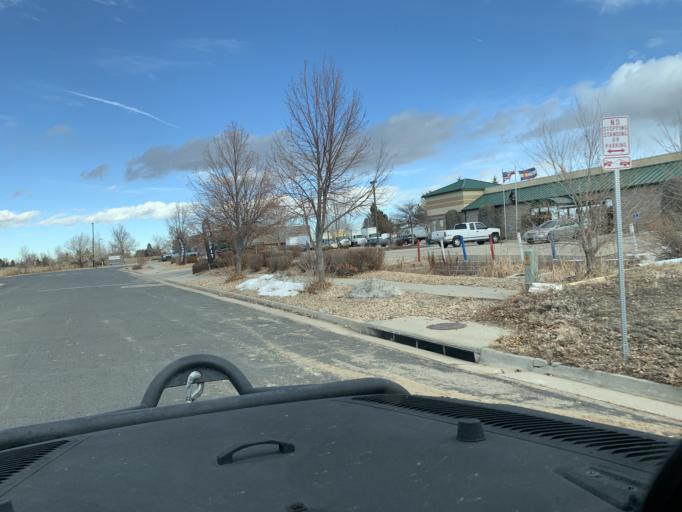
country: US
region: Colorado
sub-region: Adams County
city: Aurora
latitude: 39.7219
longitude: -104.8038
